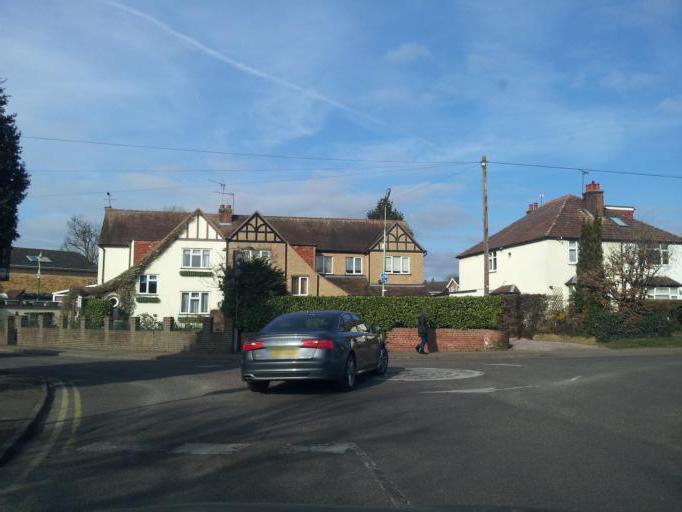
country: GB
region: England
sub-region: Hertfordshire
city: St Albans
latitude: 51.7500
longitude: -0.2928
